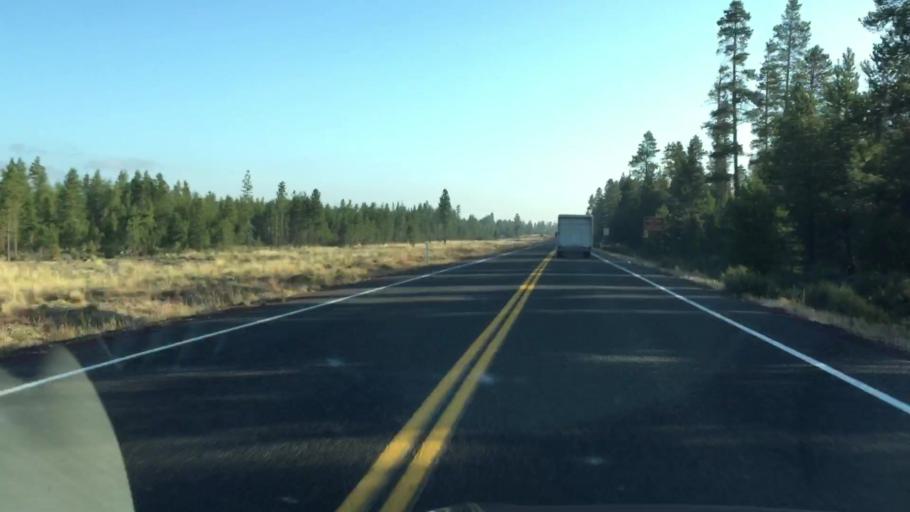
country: US
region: Oregon
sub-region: Deschutes County
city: La Pine
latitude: 43.4380
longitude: -121.7116
